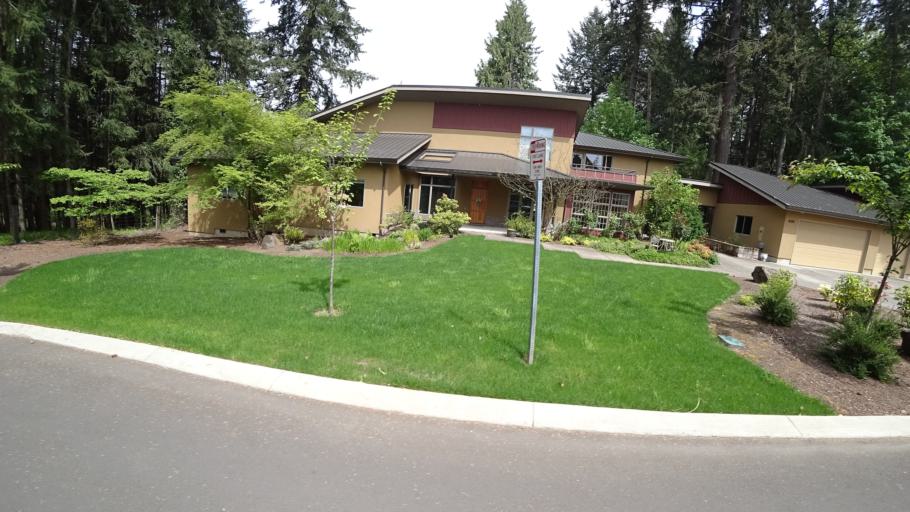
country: US
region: Oregon
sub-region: Washington County
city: Hillsboro
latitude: 45.5494
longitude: -122.9980
